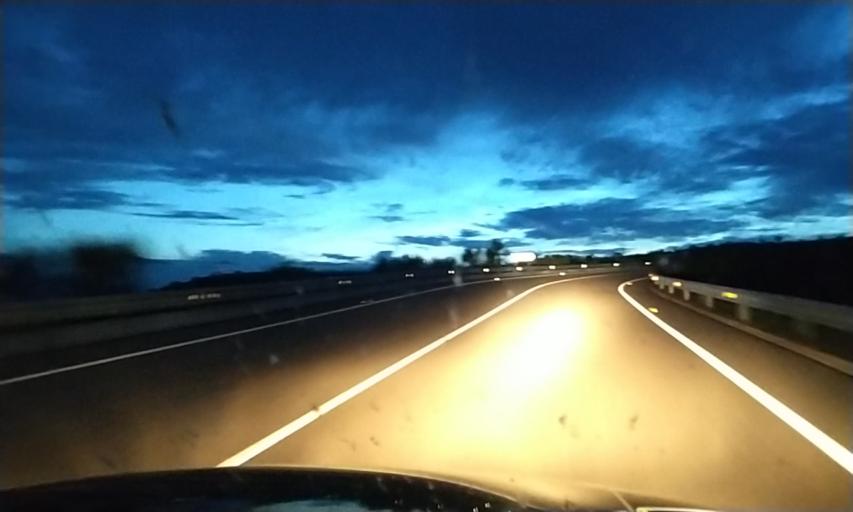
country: ES
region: Extremadura
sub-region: Provincia de Caceres
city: Plasencia
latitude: 39.9816
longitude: -6.1582
